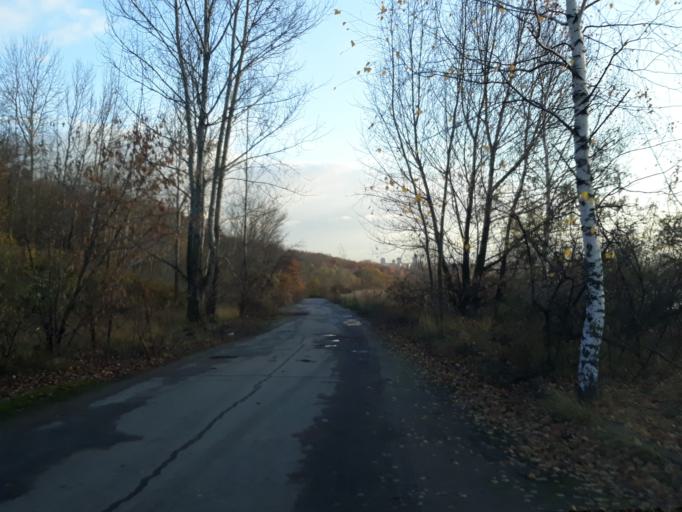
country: RU
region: Nizjnij Novgorod
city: Nizhniy Novgorod
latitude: 56.2739
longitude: 43.9698
